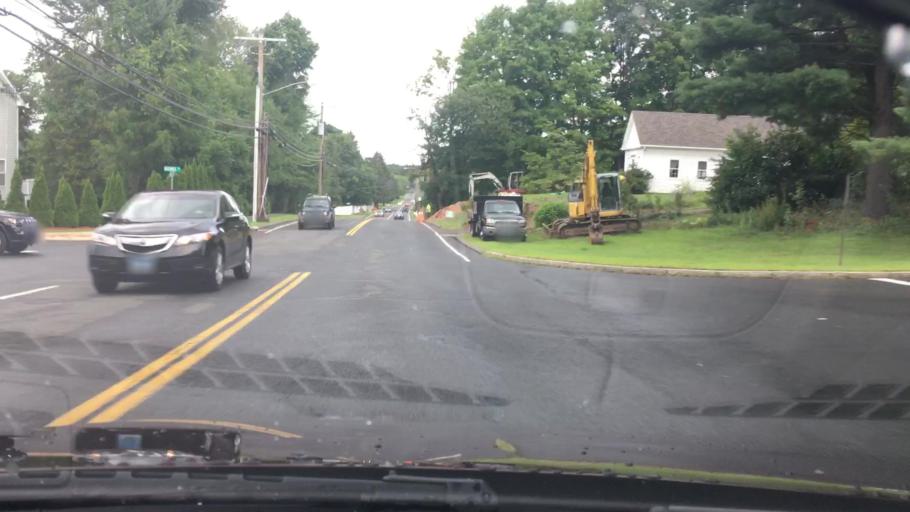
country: US
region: Connecticut
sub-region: Hartford County
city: Manchester
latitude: 41.7509
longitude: -72.5400
